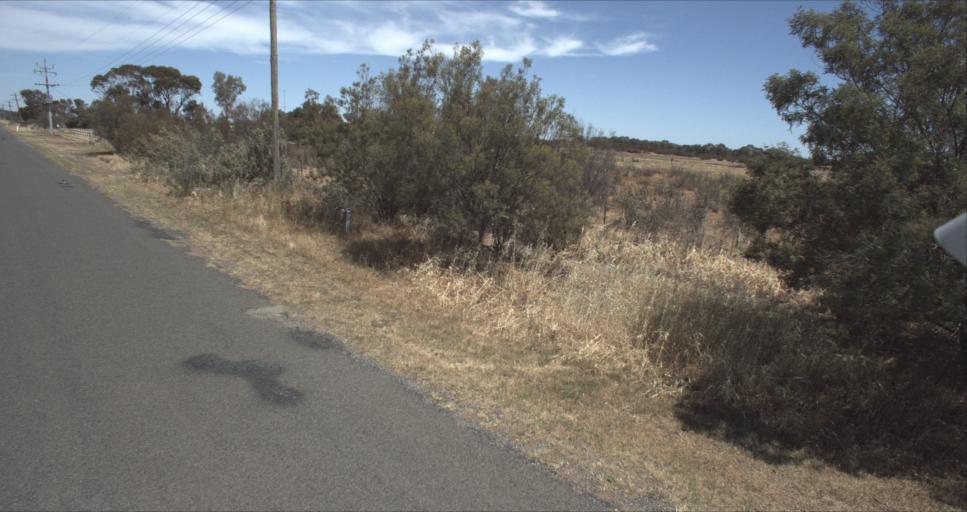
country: AU
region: New South Wales
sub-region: Leeton
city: Leeton
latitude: -34.5987
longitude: 146.4274
